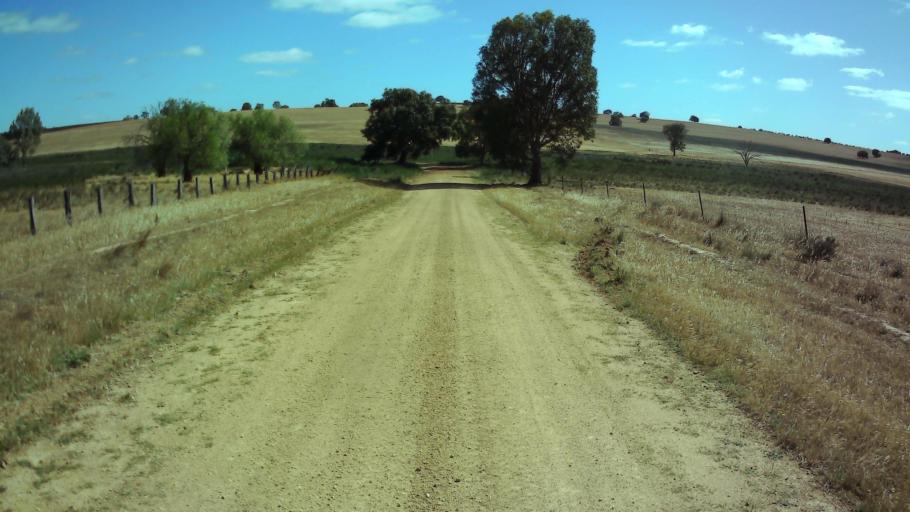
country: AU
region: New South Wales
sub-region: Weddin
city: Grenfell
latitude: -33.9810
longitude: 148.3912
